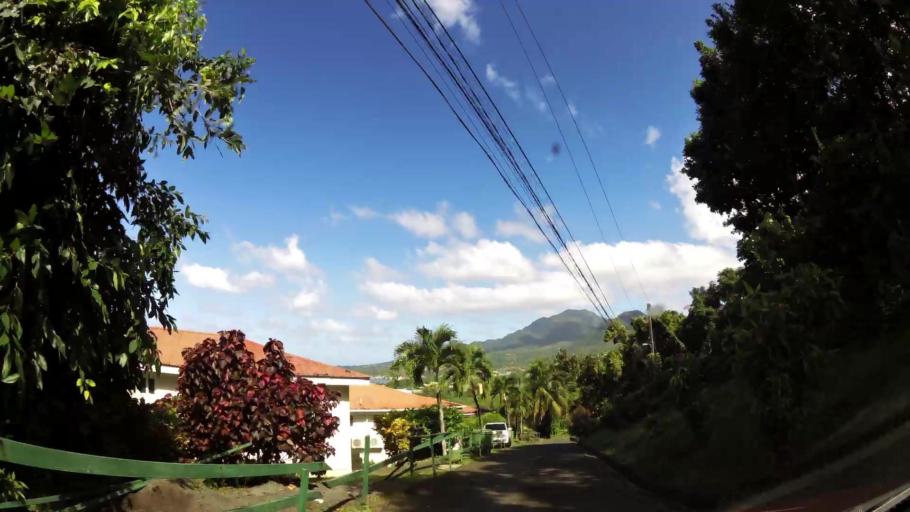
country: DM
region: Saint John
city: Portsmouth
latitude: 15.5546
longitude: -61.4552
